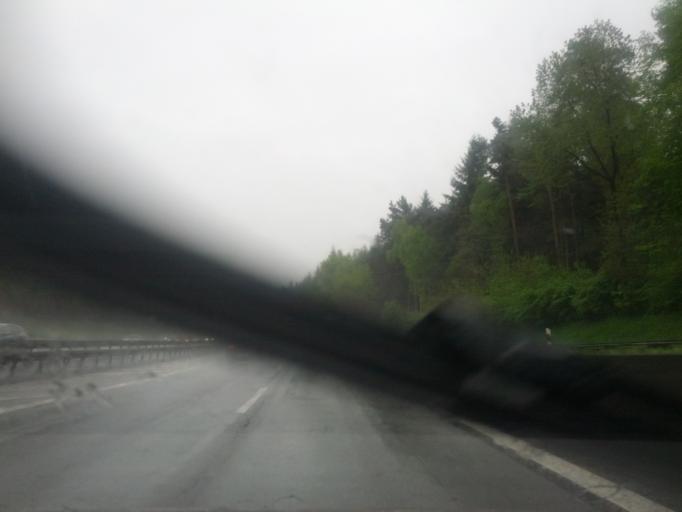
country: DE
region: North Rhine-Westphalia
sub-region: Regierungsbezirk Koln
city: Rath
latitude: 50.9473
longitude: 7.0997
